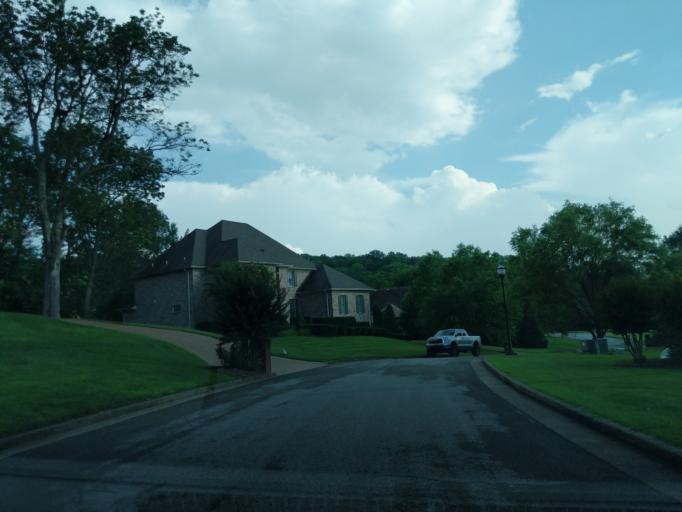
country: US
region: Tennessee
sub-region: Davidson County
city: Belle Meade
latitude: 36.0416
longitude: -86.9490
